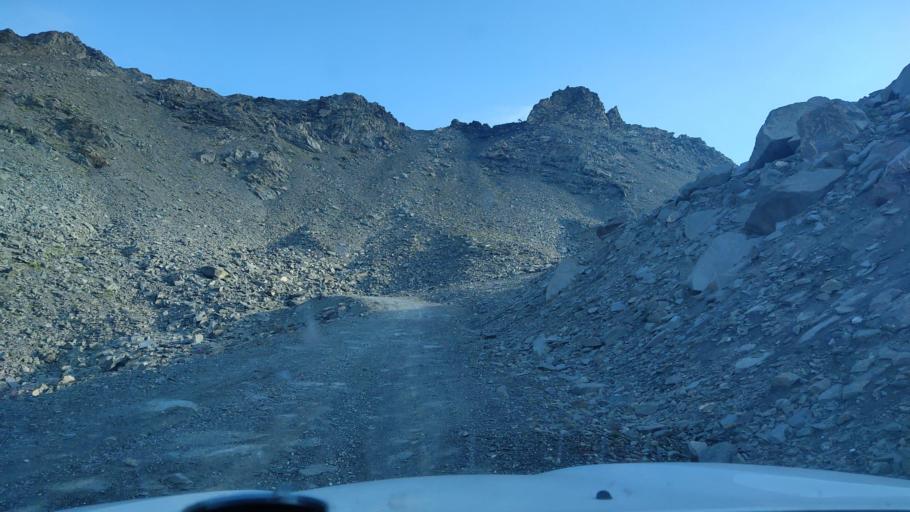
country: FR
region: Rhone-Alpes
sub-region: Departement de la Savoie
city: Val Thorens
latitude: 45.2632
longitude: 6.5728
